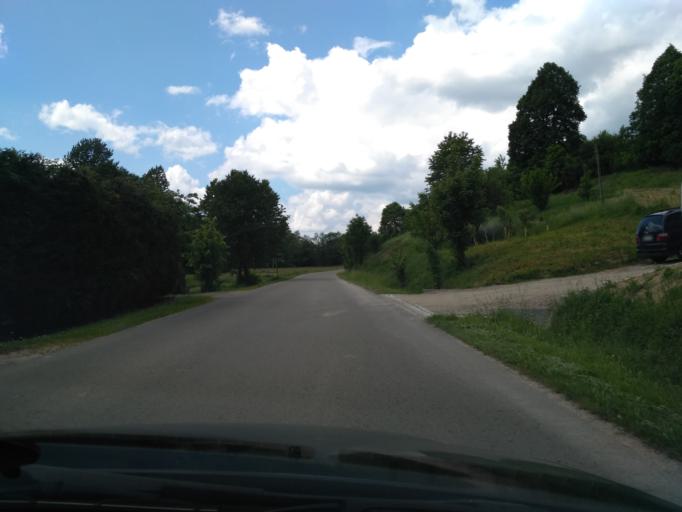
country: PL
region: Subcarpathian Voivodeship
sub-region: Powiat brzozowski
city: Wesola
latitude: 49.8073
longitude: 22.0584
